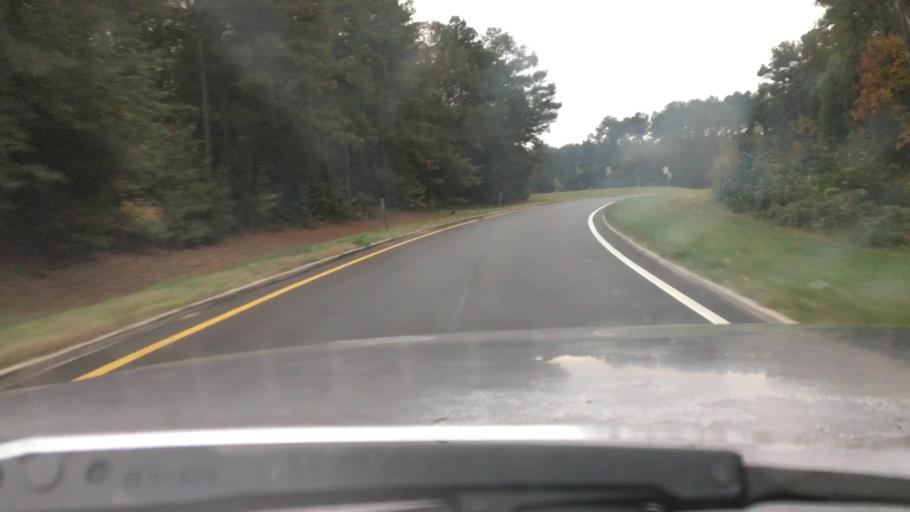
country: US
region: South Carolina
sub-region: Lexington County
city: Saint Andrews
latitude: 34.0389
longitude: -81.1135
